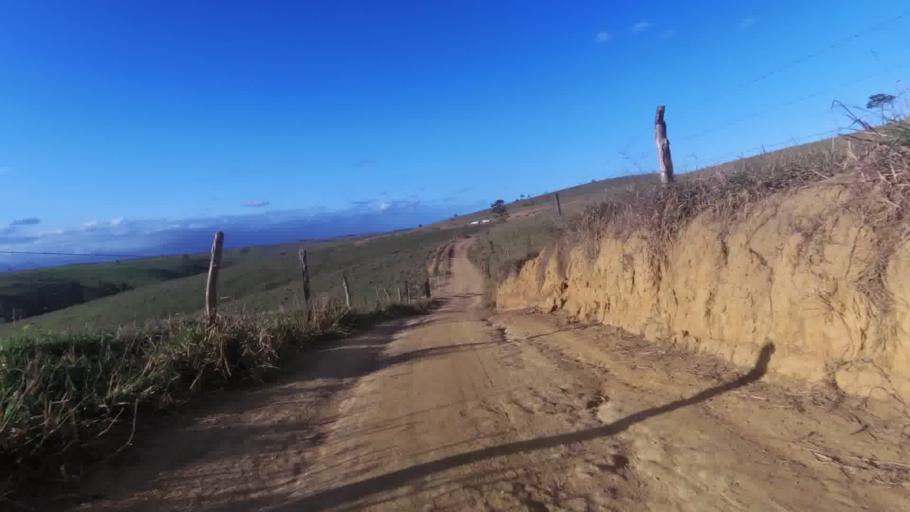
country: BR
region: Espirito Santo
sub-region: Marataizes
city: Marataizes
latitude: -21.1545
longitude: -41.0349
